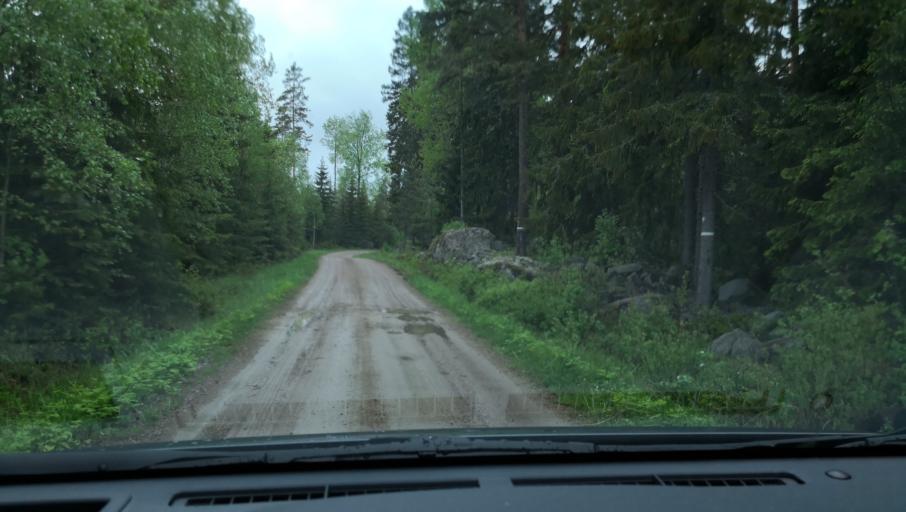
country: SE
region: Uppsala
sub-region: Enkopings Kommun
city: Orsundsbro
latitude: 59.9358
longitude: 17.3167
